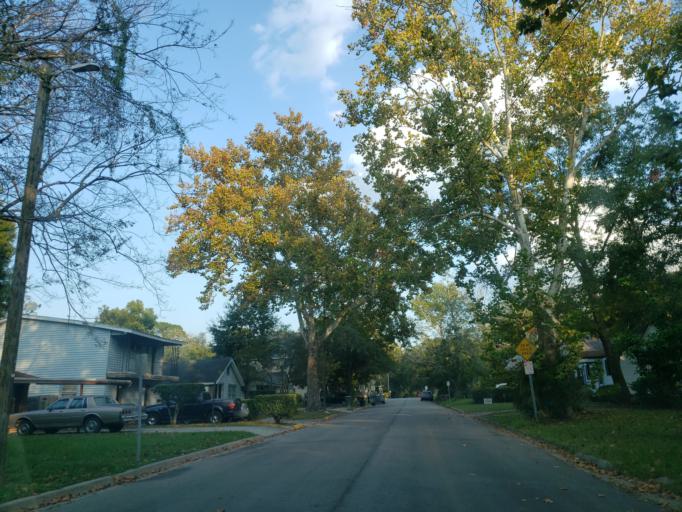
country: US
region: Georgia
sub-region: Chatham County
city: Thunderbolt
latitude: 32.0544
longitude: -81.0769
